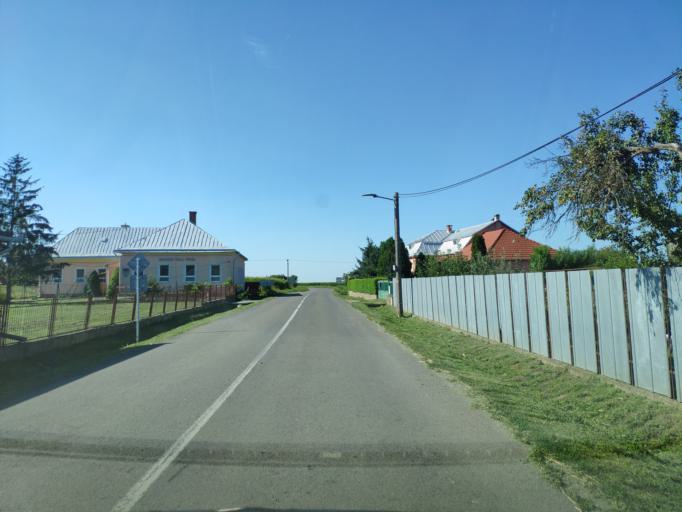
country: SK
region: Kosicky
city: Trebisov
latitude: 48.5448
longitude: 21.8838
